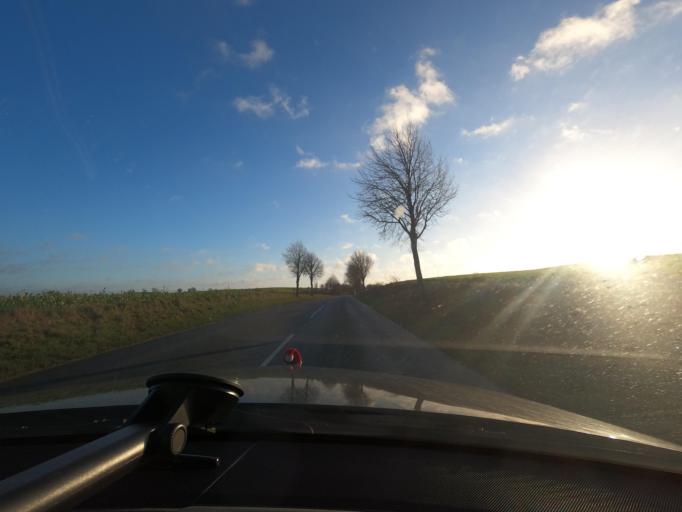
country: DK
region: South Denmark
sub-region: Sonderborg Kommune
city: Broager
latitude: 54.8946
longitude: 9.6841
